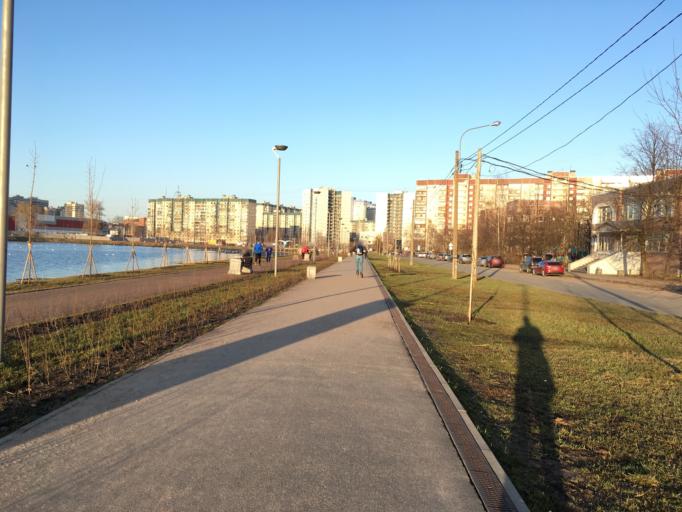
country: RU
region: St.-Petersburg
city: Komendantsky aerodrom
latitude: 60.0155
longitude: 30.2636
